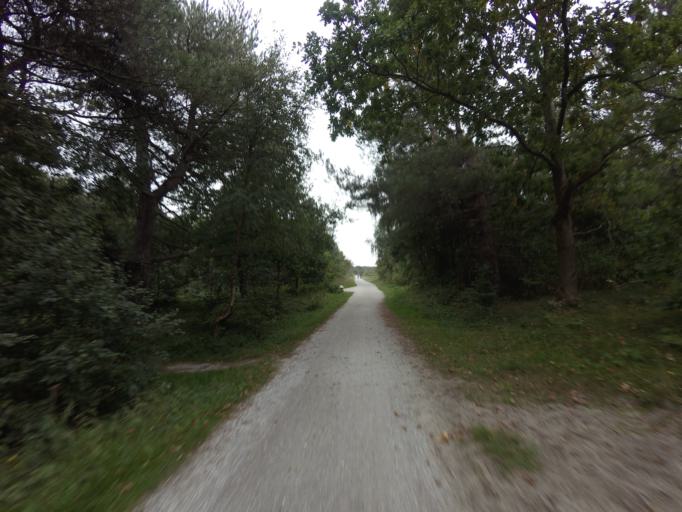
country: NL
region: Friesland
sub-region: Gemeente Schiermonnikoog
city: Schiermonnikoog
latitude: 53.4908
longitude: 6.1638
